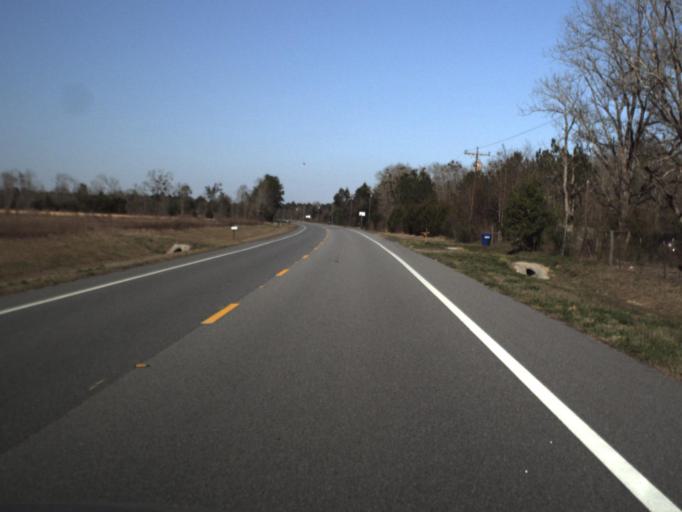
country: US
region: Florida
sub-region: Calhoun County
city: Blountstown
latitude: 30.3321
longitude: -85.2225
